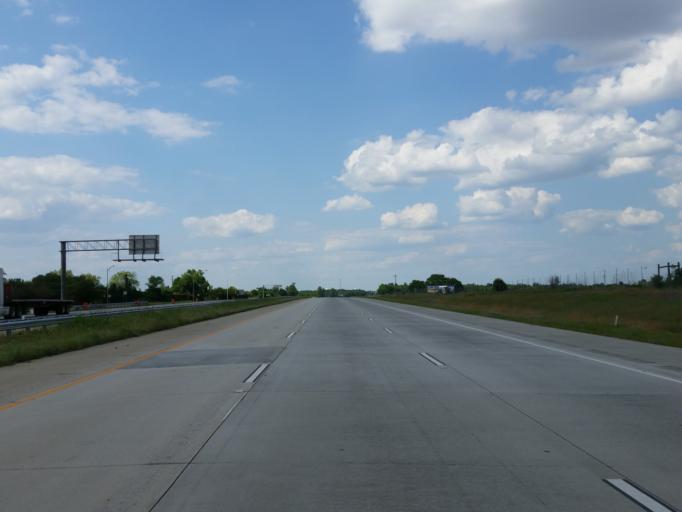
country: US
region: Georgia
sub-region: Dooly County
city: Unadilla
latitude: 32.2088
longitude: -83.7459
